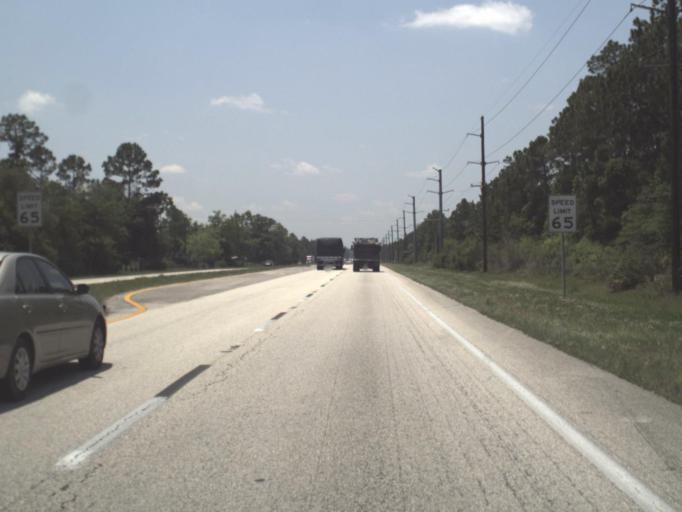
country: US
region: Florida
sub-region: Bradford County
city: Starke
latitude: 30.1031
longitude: -82.0526
